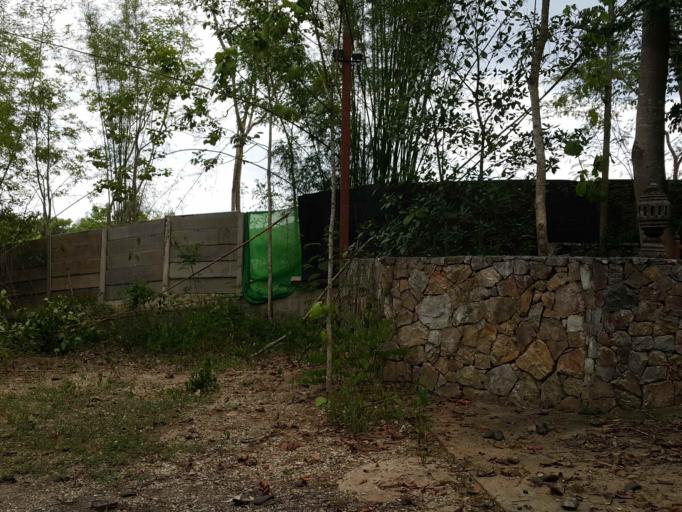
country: TH
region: Chiang Mai
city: Hang Dong
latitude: 18.7408
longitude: 98.8858
